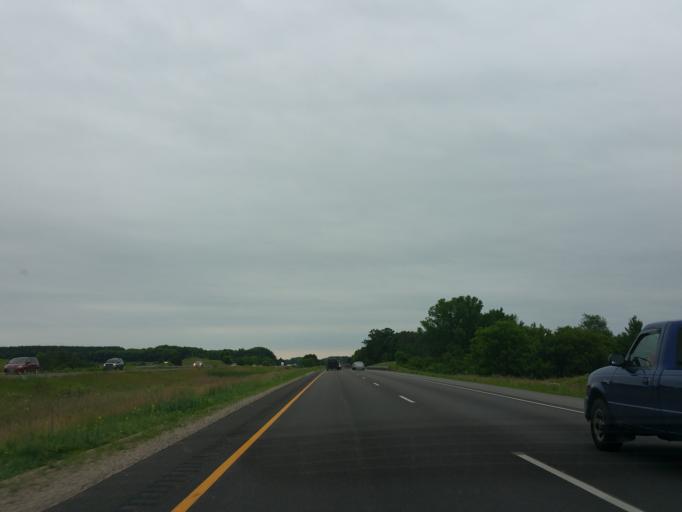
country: US
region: Wisconsin
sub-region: Eau Claire County
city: Fall Creek
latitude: 44.7119
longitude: -91.3467
